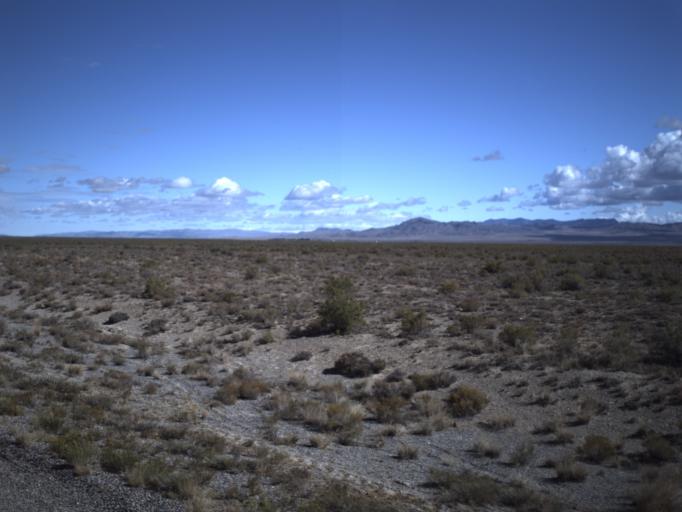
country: US
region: Nevada
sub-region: White Pine County
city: McGill
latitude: 39.0043
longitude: -114.0349
